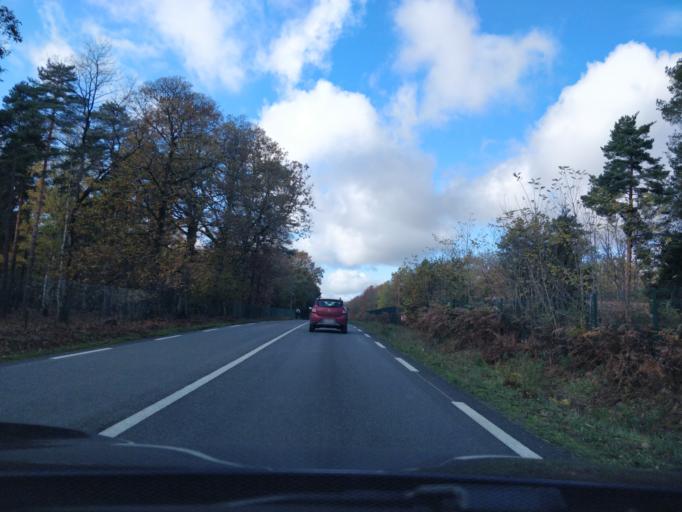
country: FR
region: Ile-de-France
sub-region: Departement de l'Essonne
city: Bruyeres-le-Chatel
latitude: 48.6054
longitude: 2.2012
